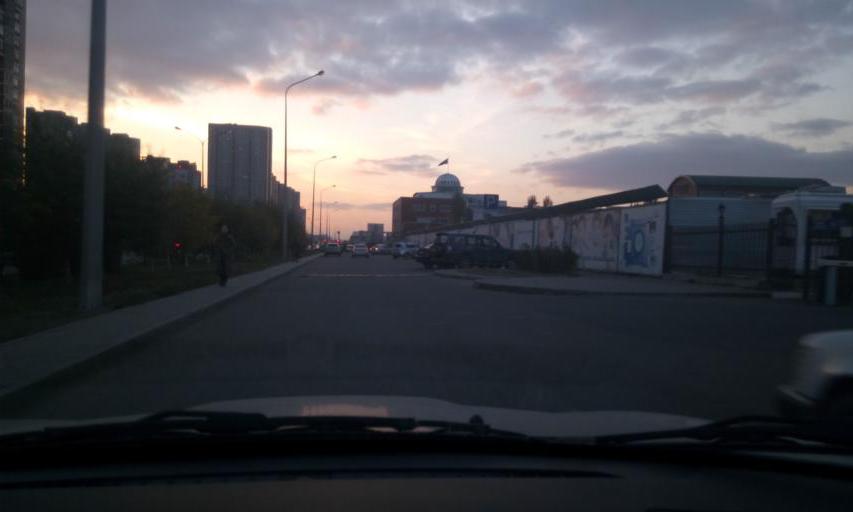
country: KZ
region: Astana Qalasy
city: Astana
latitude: 51.1263
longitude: 71.4802
